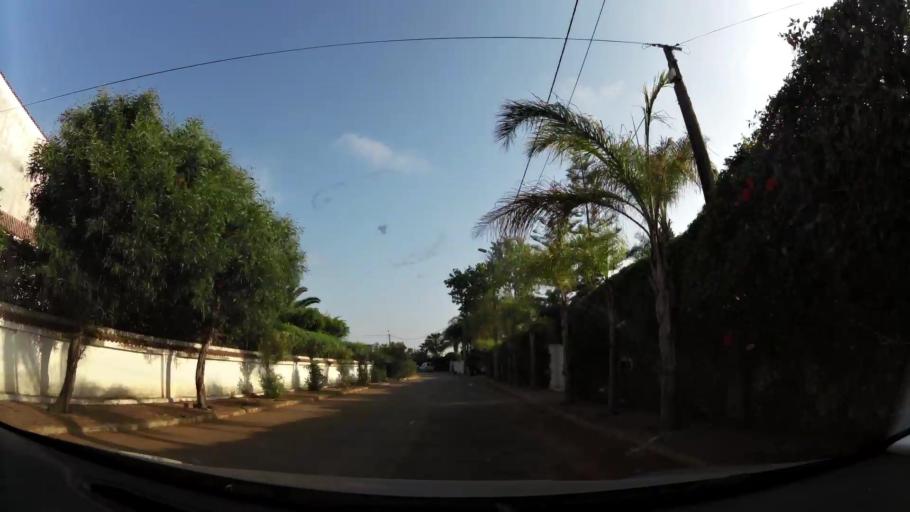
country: MA
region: Rabat-Sale-Zemmour-Zaer
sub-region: Rabat
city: Rabat
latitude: 33.9419
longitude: -6.8097
